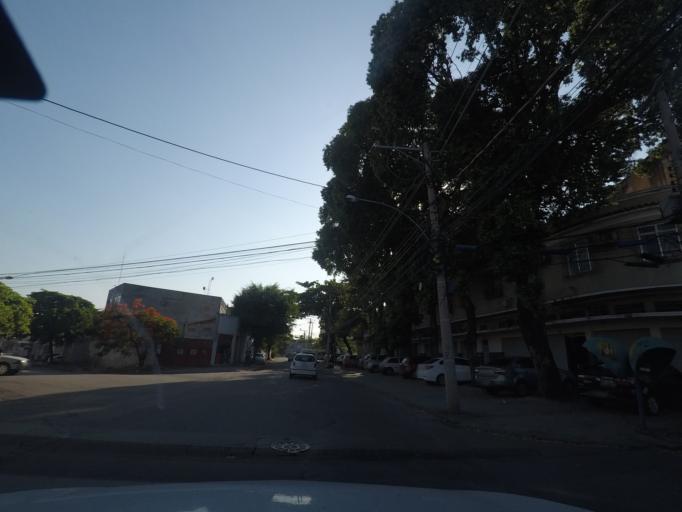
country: BR
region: Rio de Janeiro
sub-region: Rio De Janeiro
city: Rio de Janeiro
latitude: -22.8455
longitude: -43.2522
